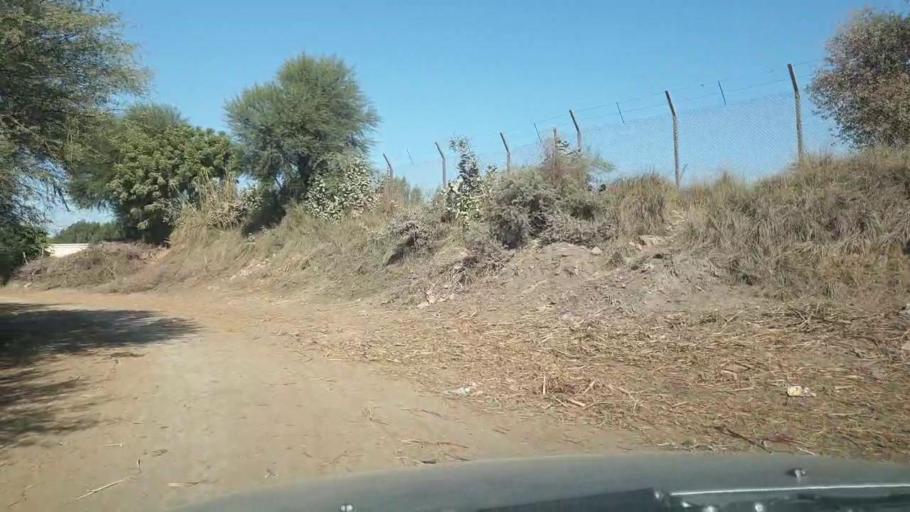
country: PK
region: Sindh
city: Ghotki
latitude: 28.1018
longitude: 69.3421
